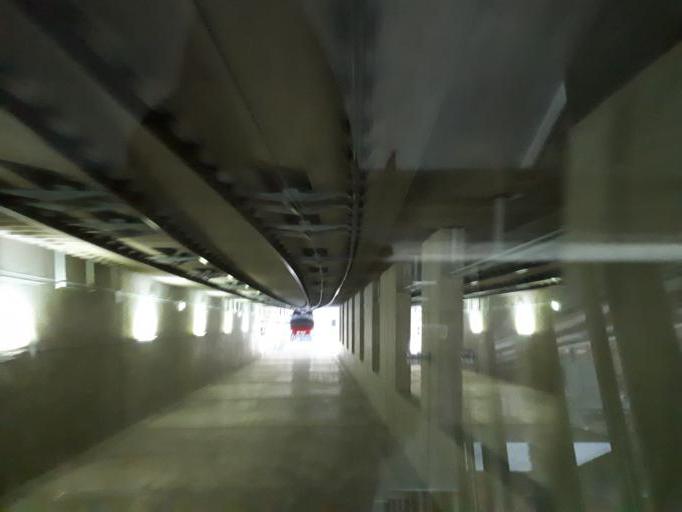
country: LU
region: Luxembourg
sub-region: Canton de Luxembourg
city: Luxembourg
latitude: 49.6189
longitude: 6.1338
